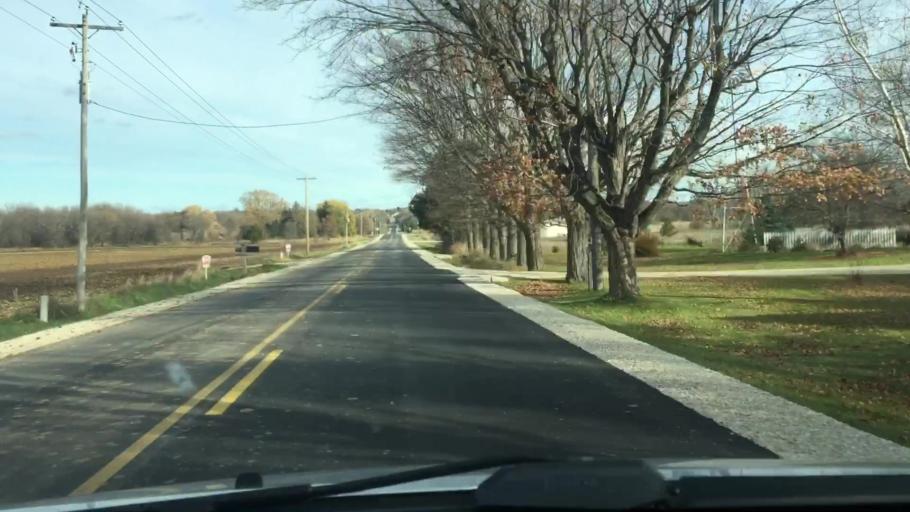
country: US
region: Wisconsin
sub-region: Kewaunee County
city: Algoma
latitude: 44.6901
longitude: -87.5039
